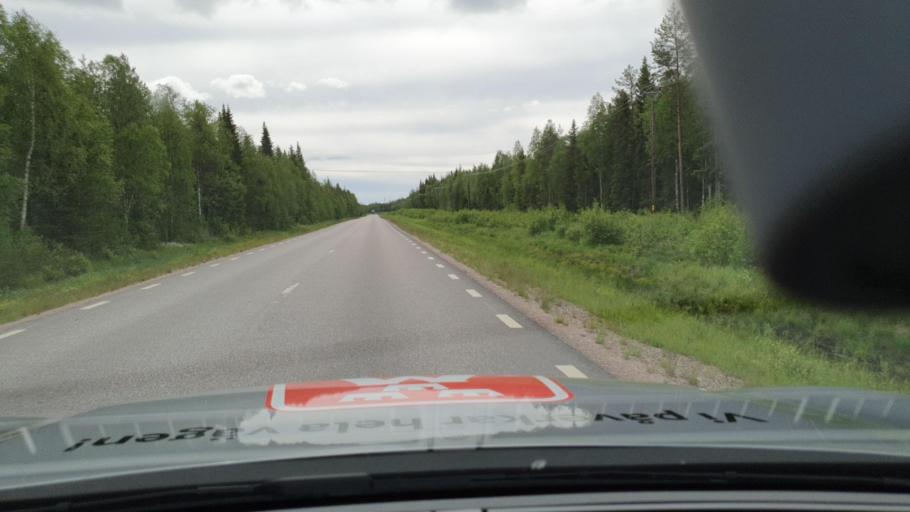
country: SE
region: Norrbotten
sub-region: Kalix Kommun
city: Kalix
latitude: 65.9063
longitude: 23.4570
